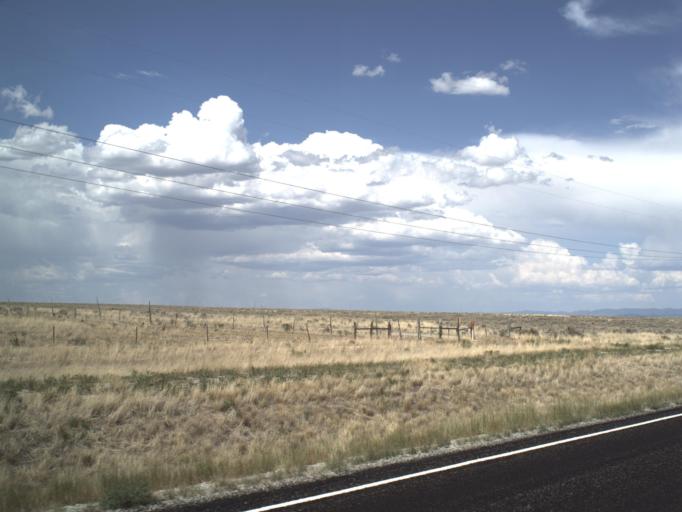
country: US
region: Idaho
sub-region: Power County
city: American Falls
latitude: 41.9671
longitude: -113.0816
